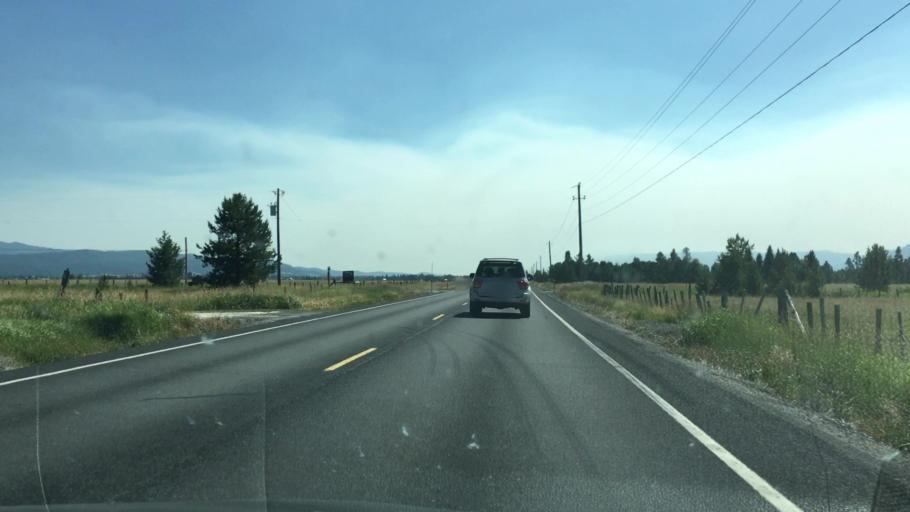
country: US
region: Idaho
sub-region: Valley County
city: McCall
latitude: 44.7609
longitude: -116.0782
